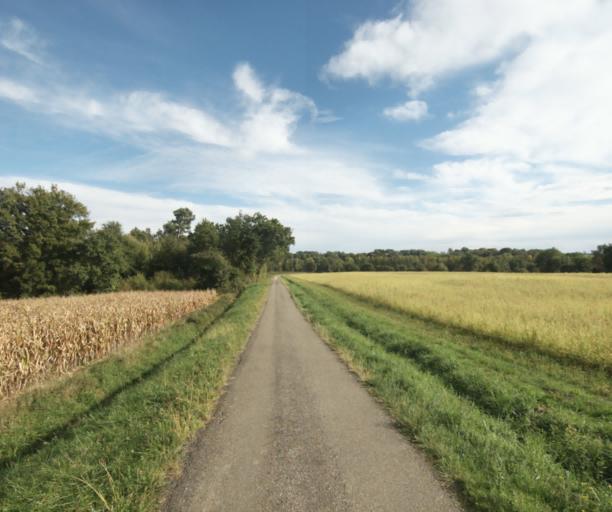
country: FR
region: Midi-Pyrenees
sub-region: Departement du Gers
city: Cazaubon
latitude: 43.8785
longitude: -0.1214
